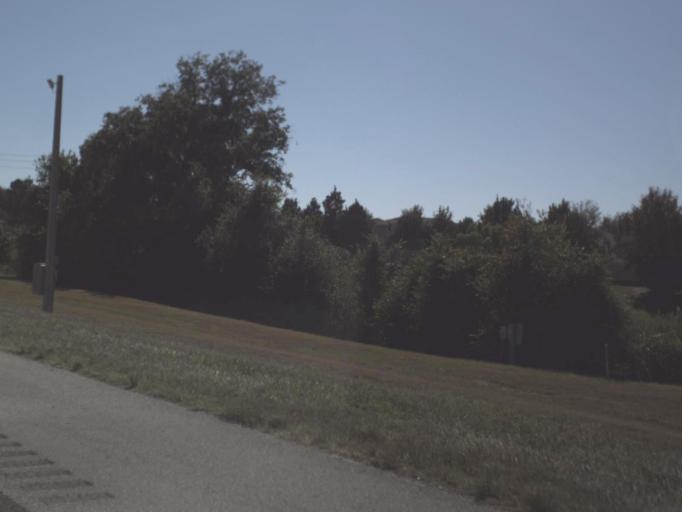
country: US
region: Florida
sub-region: Lake County
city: Montverde
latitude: 28.5743
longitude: -81.6988
